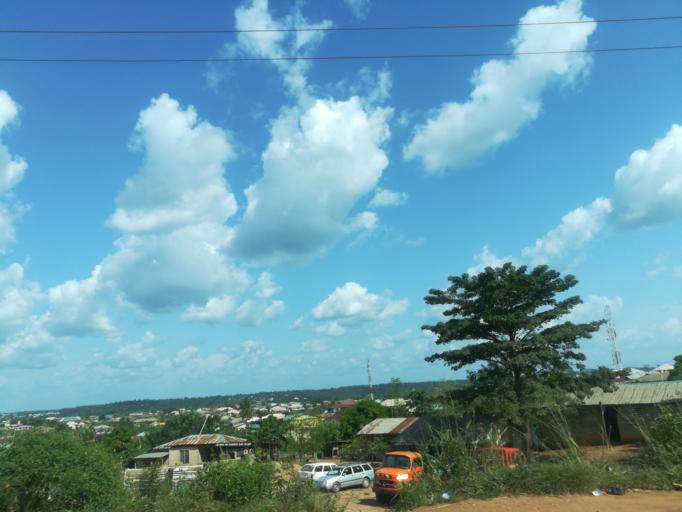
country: NG
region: Oyo
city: Lalupon
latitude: 7.4343
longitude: 4.0048
